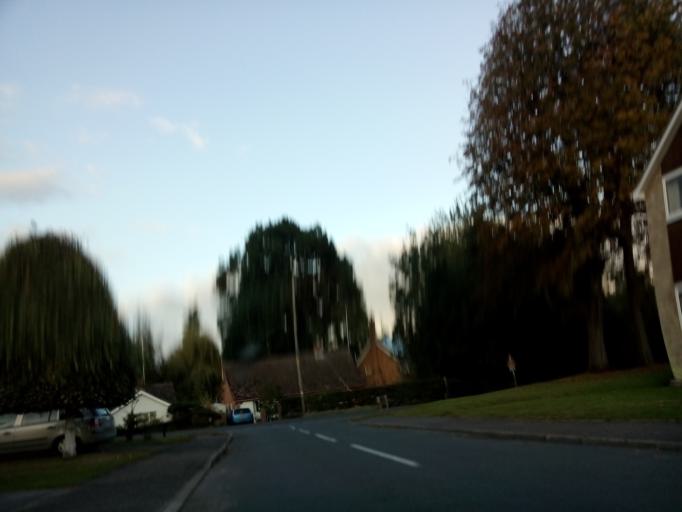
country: GB
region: England
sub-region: Suffolk
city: Bramford
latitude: 52.0614
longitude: 1.0991
